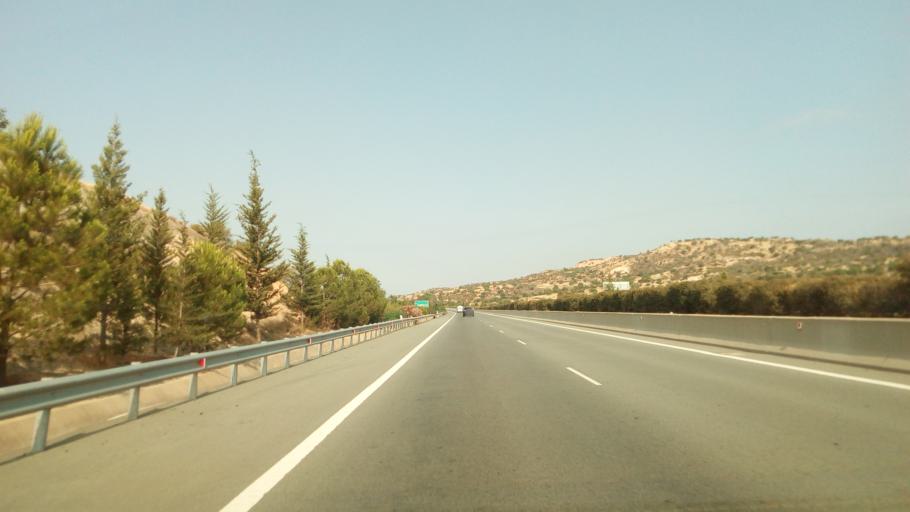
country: CY
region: Limassol
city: Pissouri
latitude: 34.6856
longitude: 32.7404
